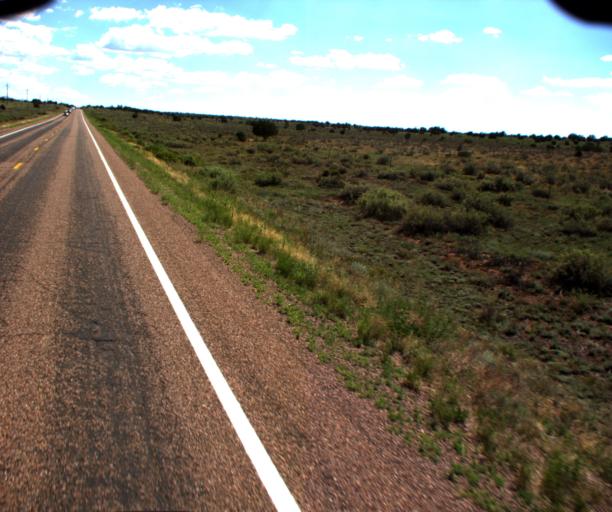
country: US
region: Arizona
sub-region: Coconino County
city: Williams
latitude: 35.5688
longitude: -112.1556
